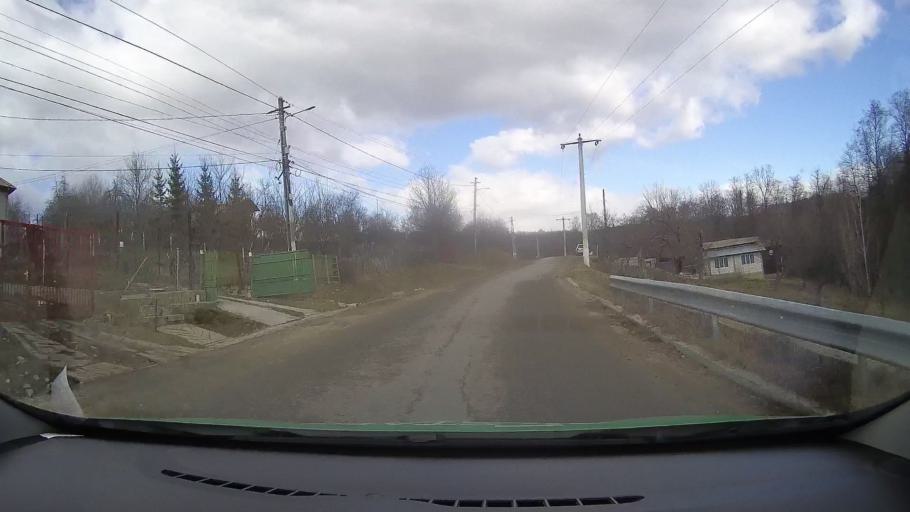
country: RO
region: Dambovita
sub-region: Comuna Buciumeni
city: Buciumeni
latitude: 45.1315
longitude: 25.4679
